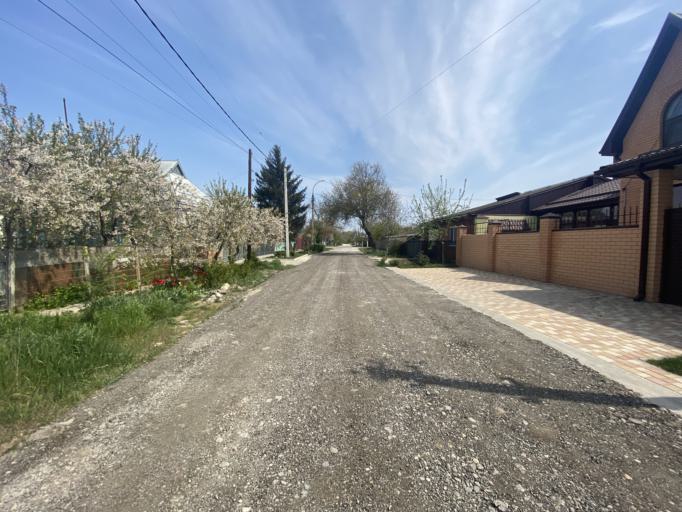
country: RU
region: Krasnodarskiy
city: Slavyansk-na-Kubani
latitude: 45.2696
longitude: 38.1222
